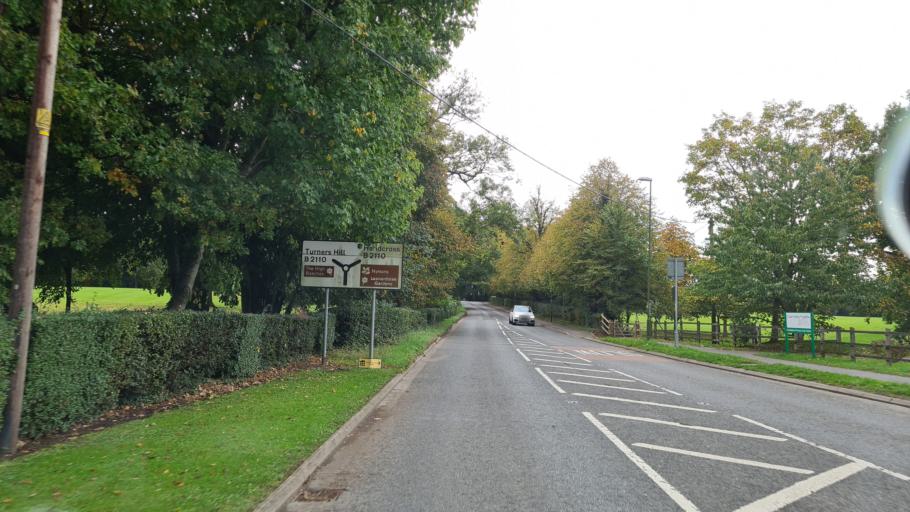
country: GB
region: England
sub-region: West Sussex
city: Broadfield
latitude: 51.0593
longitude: -0.1991
